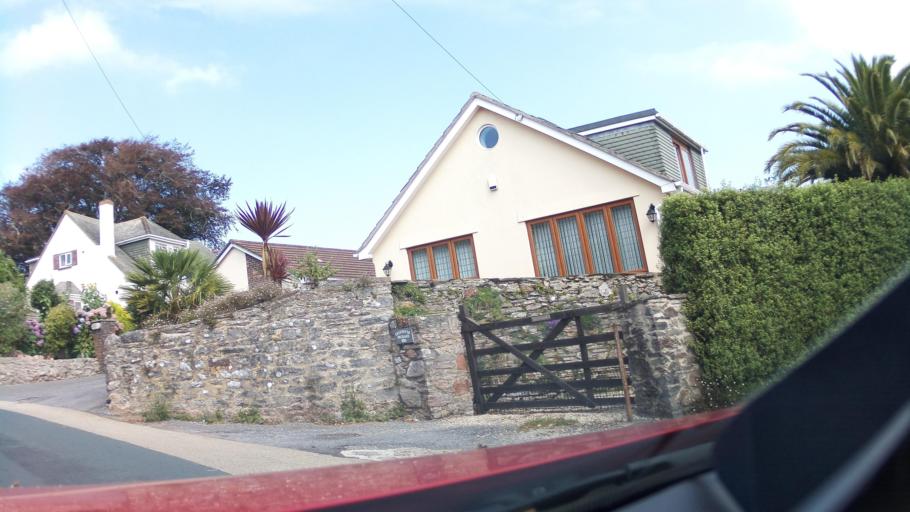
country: GB
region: England
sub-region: Borough of Torbay
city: Brixham
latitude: 50.3875
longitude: -3.5228
